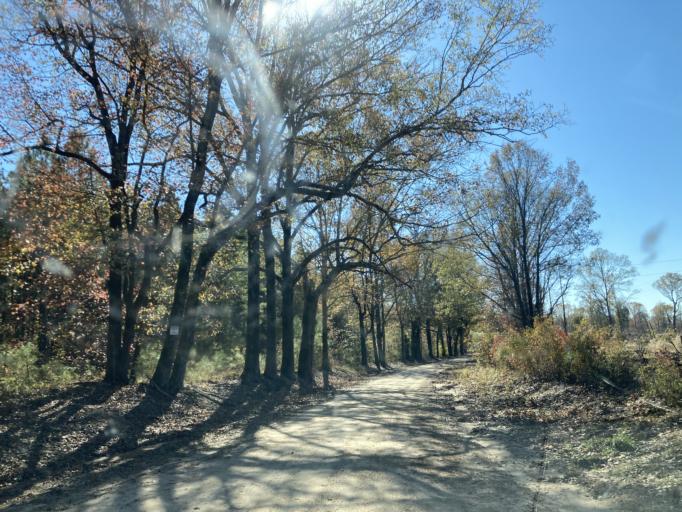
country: US
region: Mississippi
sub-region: Hinds County
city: Lynchburg
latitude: 32.5727
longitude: -90.5470
